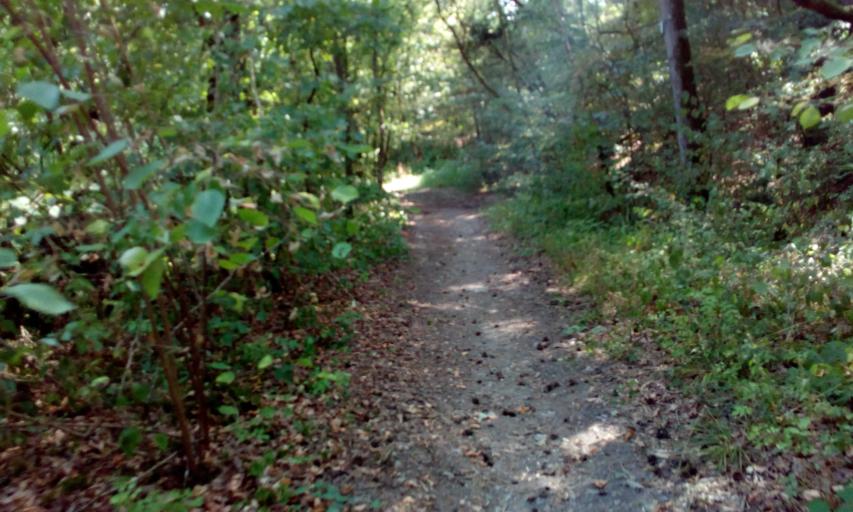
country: BE
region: Wallonia
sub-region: Province du Luxembourg
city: Wellin
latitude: 50.1096
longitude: 5.1302
